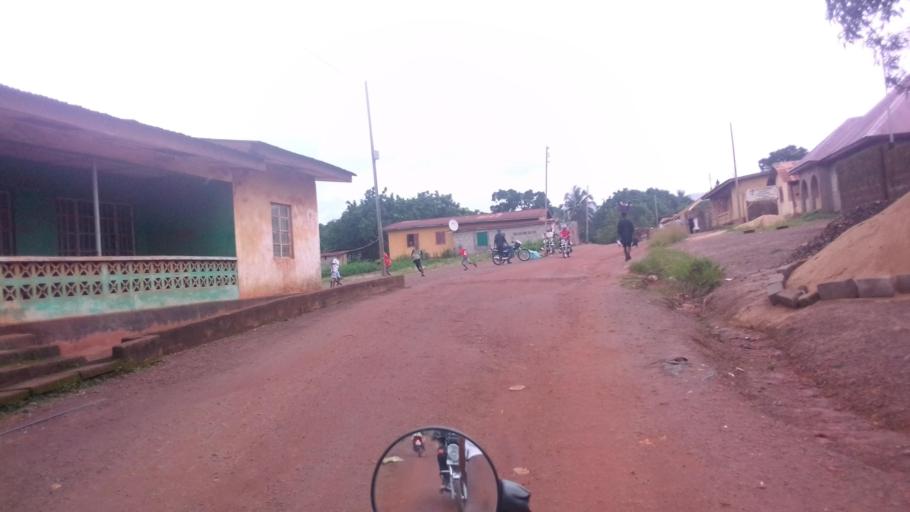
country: SL
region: Eastern Province
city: Kenema
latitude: 7.8711
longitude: -11.1787
